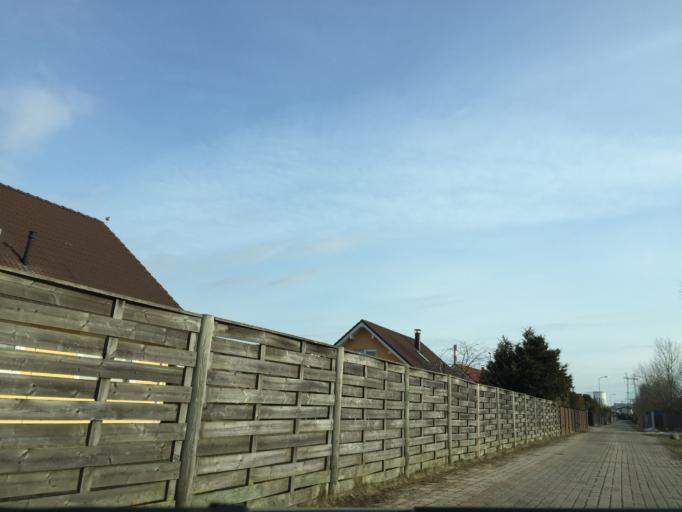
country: LV
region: Stopini
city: Ulbroka
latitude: 56.9283
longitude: 24.2583
